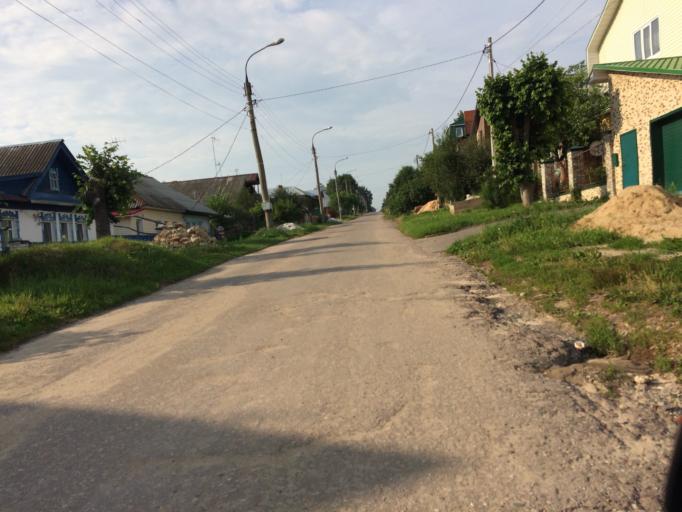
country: RU
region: Mariy-El
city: Yoshkar-Ola
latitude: 56.6180
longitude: 47.9446
